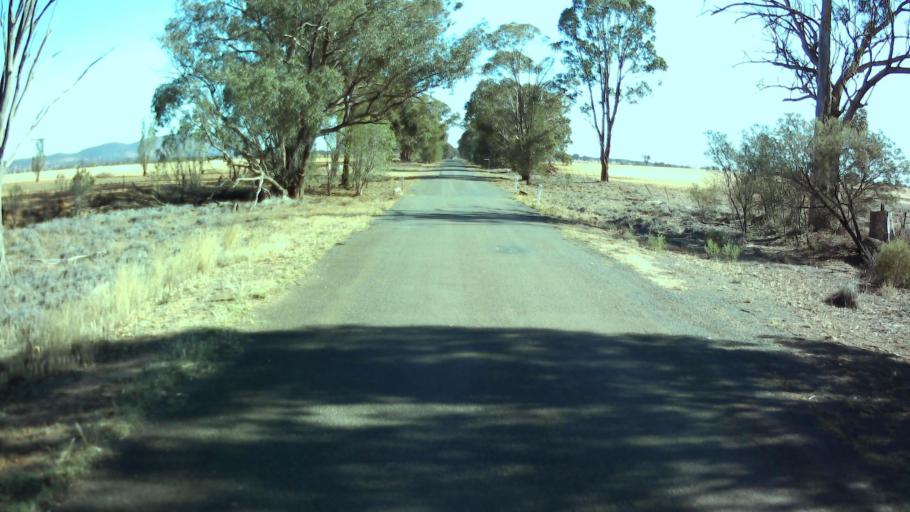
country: AU
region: New South Wales
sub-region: Weddin
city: Grenfell
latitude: -33.8066
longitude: 147.9547
